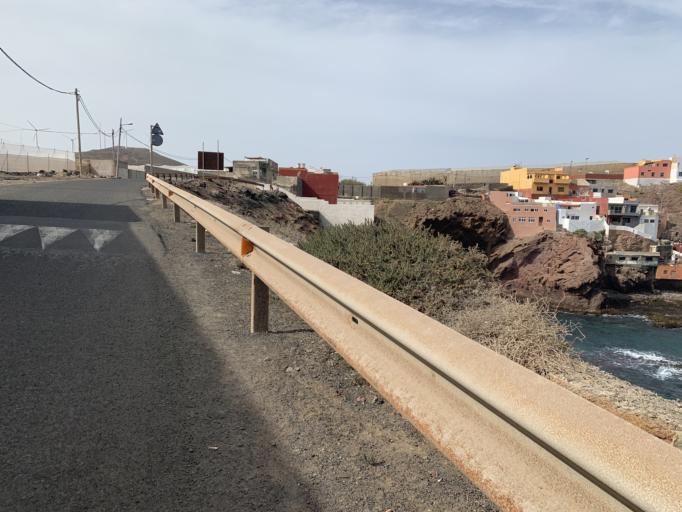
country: ES
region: Canary Islands
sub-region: Provincia de Las Palmas
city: Galdar
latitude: 28.1594
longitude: -15.6718
